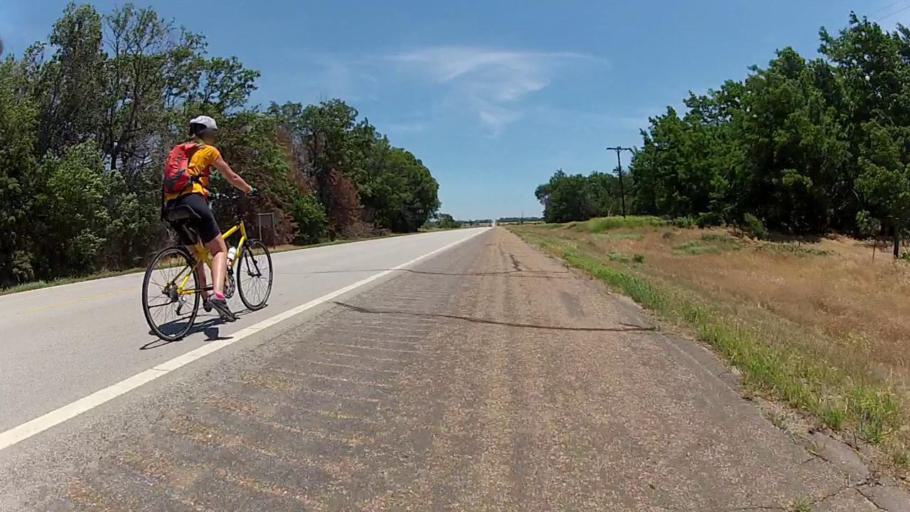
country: US
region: Kansas
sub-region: Barber County
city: Medicine Lodge
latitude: 37.2533
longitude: -98.3249
